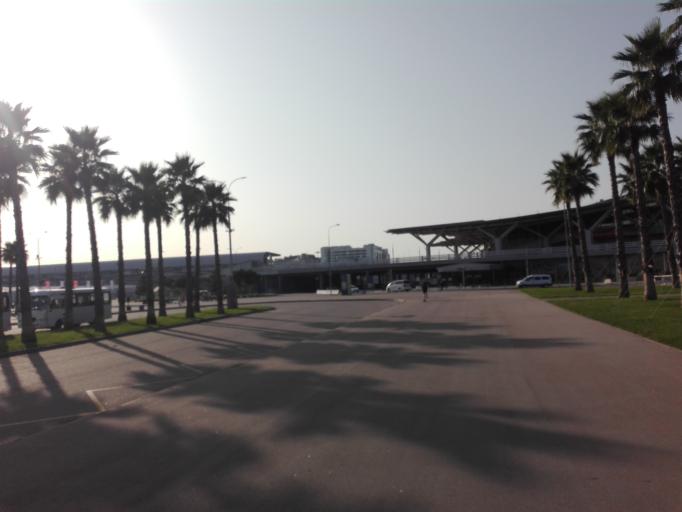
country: RU
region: Krasnodarskiy
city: Vysokoye
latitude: 43.4105
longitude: 39.9751
